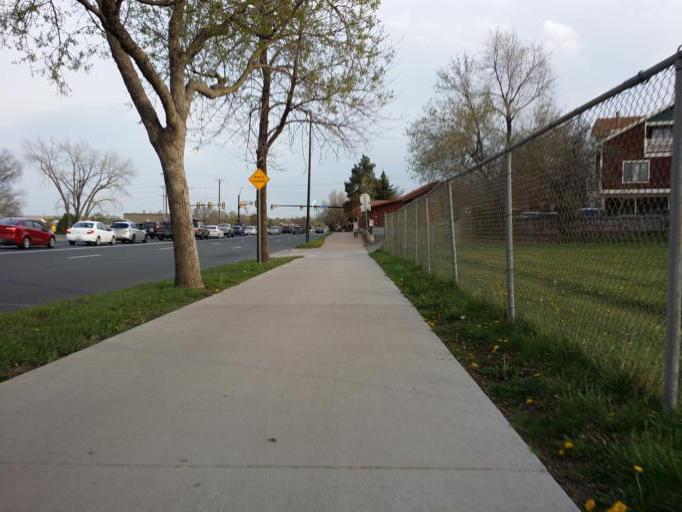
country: US
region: Colorado
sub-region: Boulder County
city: Boulder
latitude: 40.0011
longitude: -105.2646
